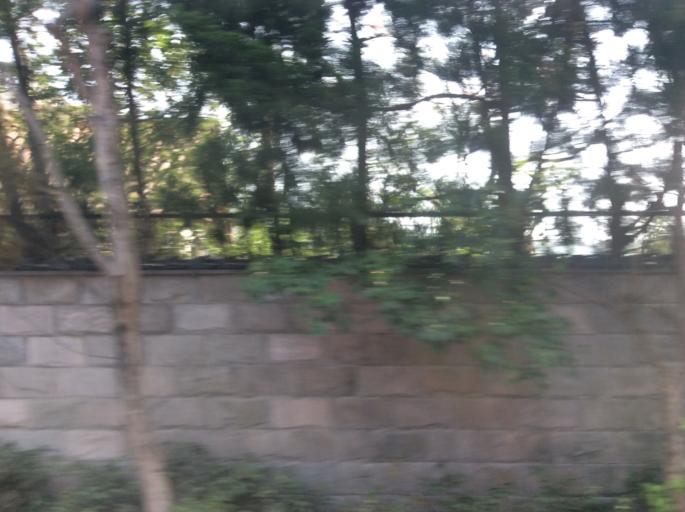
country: TW
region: Taipei
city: Taipei
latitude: 25.1224
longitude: 121.5520
